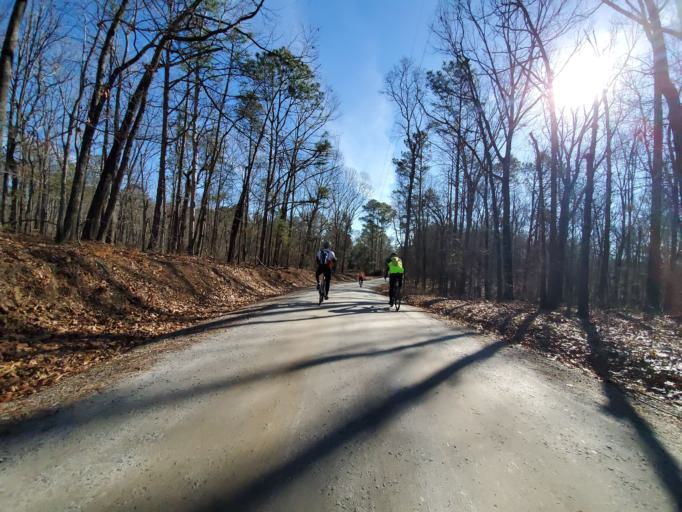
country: US
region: Georgia
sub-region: Fulton County
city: Chattahoochee Hills
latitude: 33.5634
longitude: -84.7845
